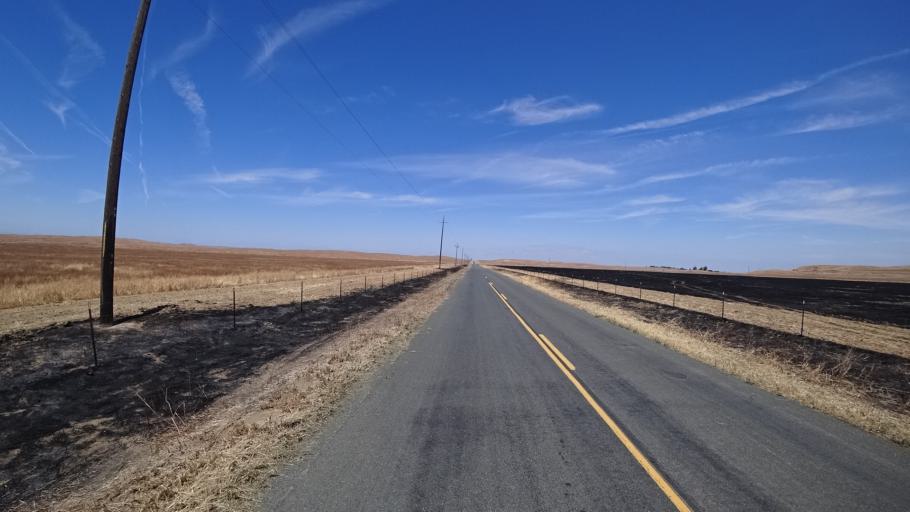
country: US
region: California
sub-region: Kings County
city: Kettleman City
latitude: 35.8369
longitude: -119.9153
